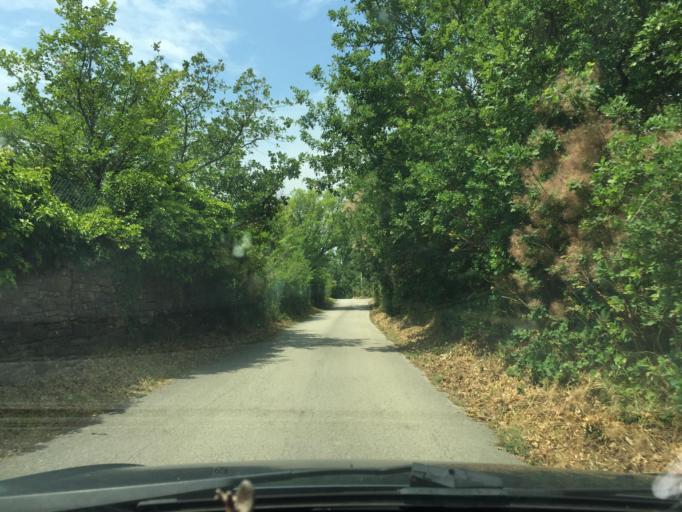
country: IT
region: Friuli Venezia Giulia
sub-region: Provincia di Trieste
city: Domio
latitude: 45.6003
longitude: 13.8186
